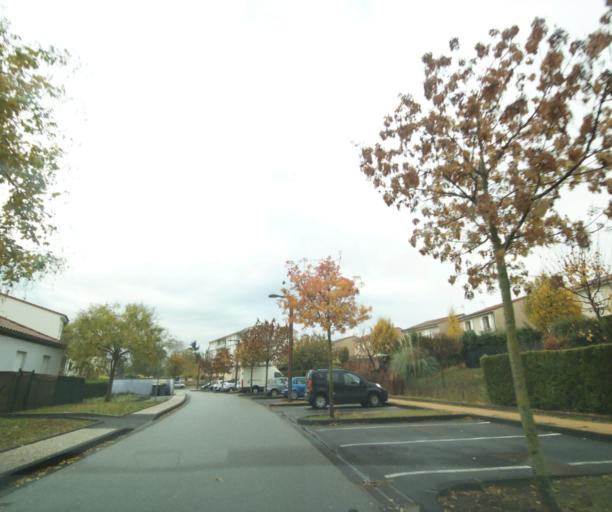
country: FR
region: Auvergne
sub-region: Departement du Puy-de-Dome
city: Cournon-d'Auvergne
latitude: 45.7413
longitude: 3.2084
